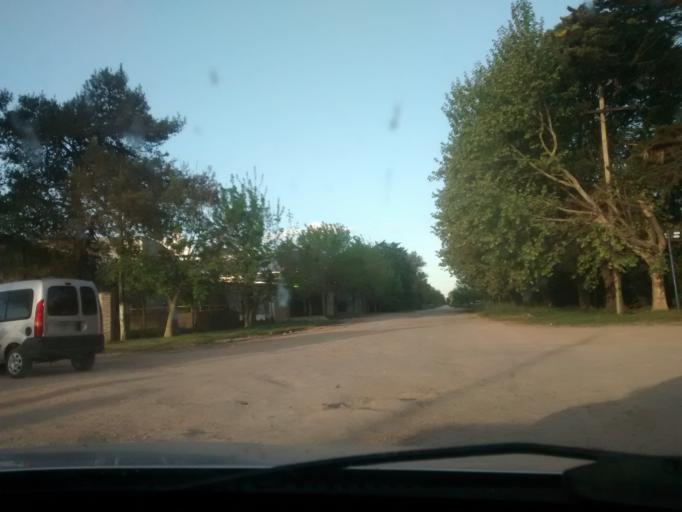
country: AR
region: Buenos Aires
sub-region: Partido de Brandsen
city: Brandsen
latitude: -35.1738
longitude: -58.2197
